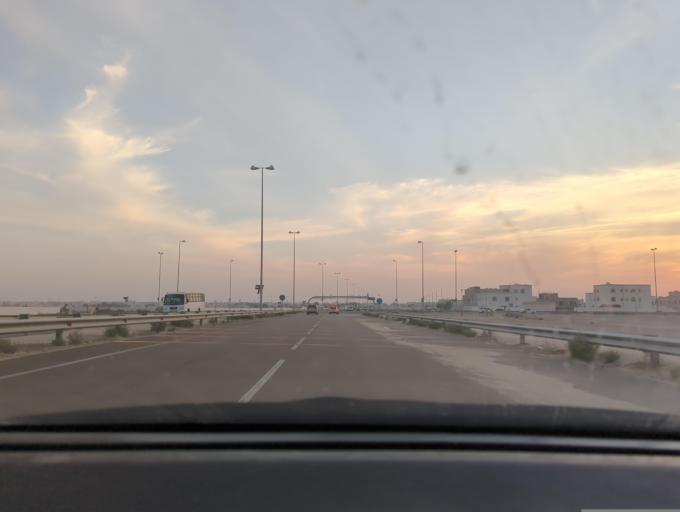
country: AE
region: Abu Dhabi
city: Abu Dhabi
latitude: 24.3331
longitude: 54.6496
